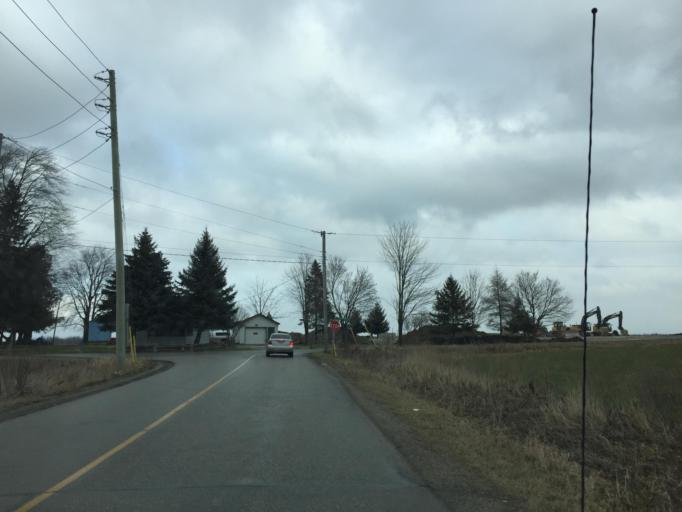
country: CA
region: Ontario
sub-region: Wellington County
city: Guelph
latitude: 43.5028
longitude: -80.3417
